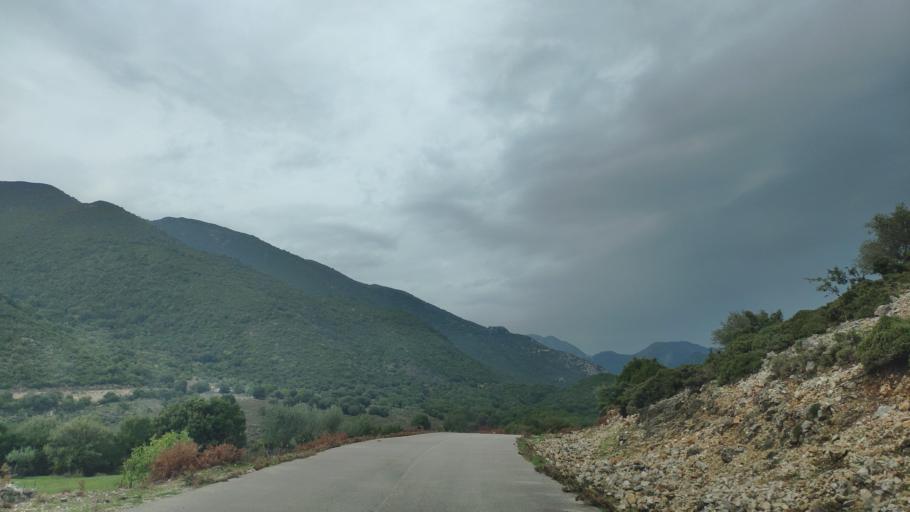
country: GR
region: Epirus
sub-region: Nomos Thesprotias
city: Paramythia
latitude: 39.3857
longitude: 20.6246
